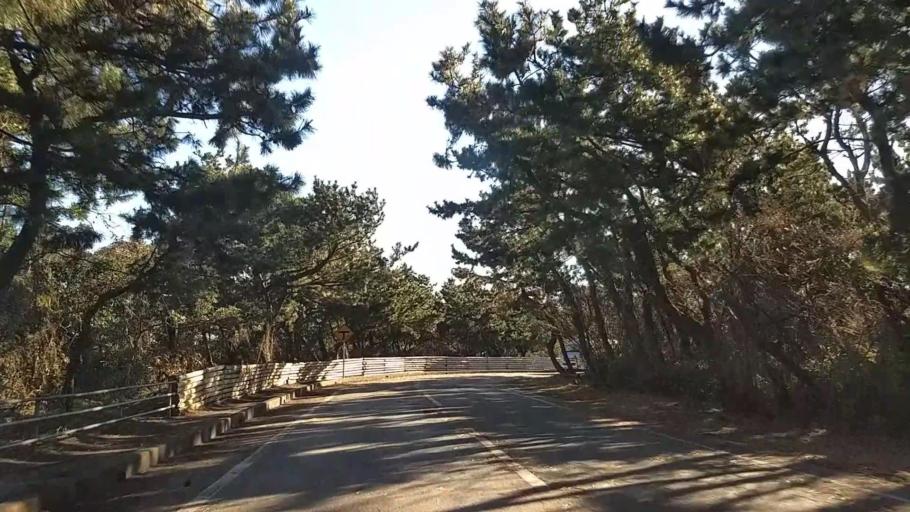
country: JP
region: Chiba
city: Futtsu
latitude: 35.3128
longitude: 139.7887
